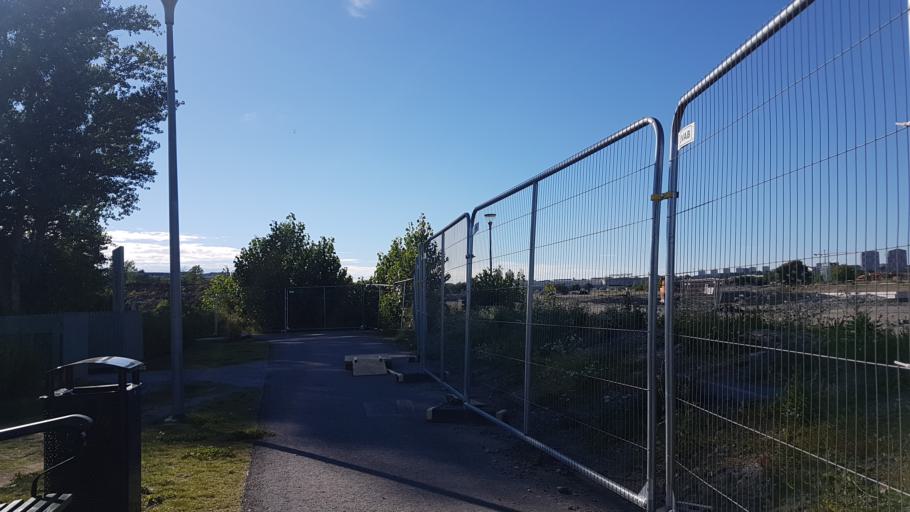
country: SE
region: Stockholm
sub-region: Stockholms Kommun
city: Arsta
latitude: 59.2899
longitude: 18.0487
